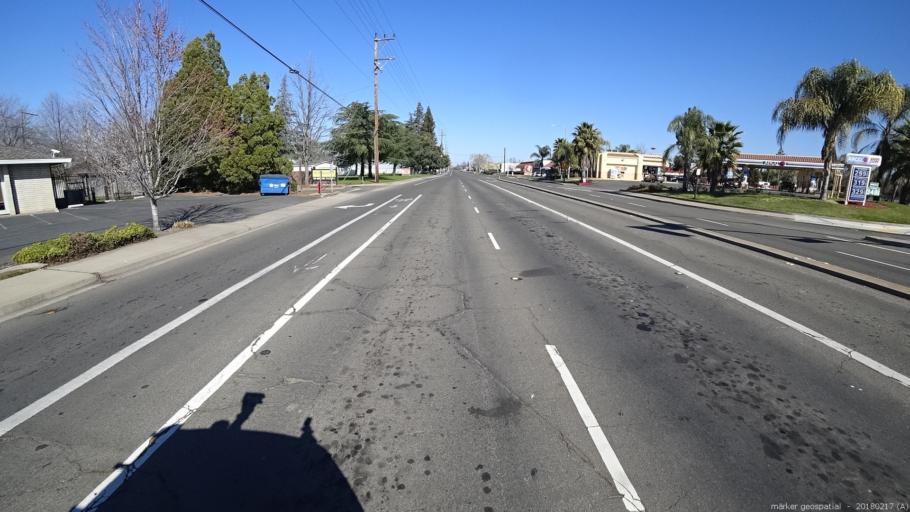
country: US
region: California
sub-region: Sacramento County
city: Orangevale
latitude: 38.6723
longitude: -121.2026
